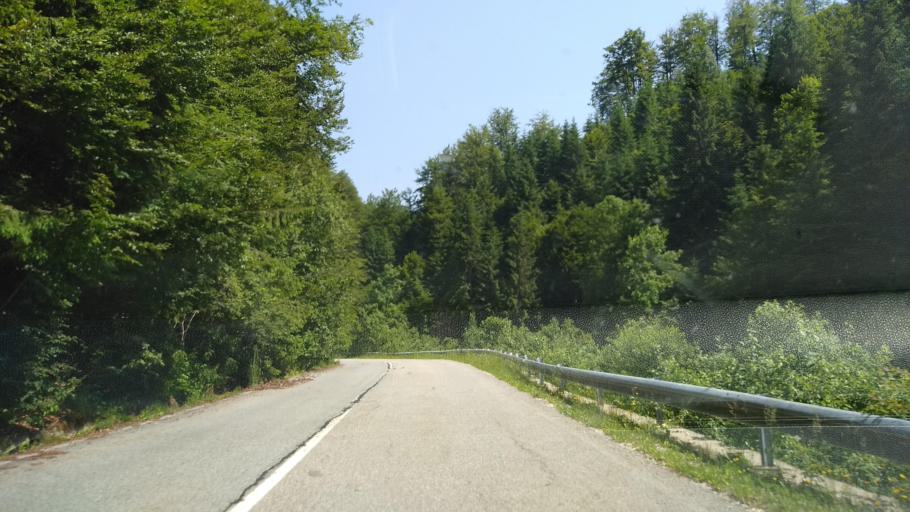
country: RO
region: Gorj
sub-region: Comuna Runcu
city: Valea Mare
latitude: 45.2762
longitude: 22.9379
